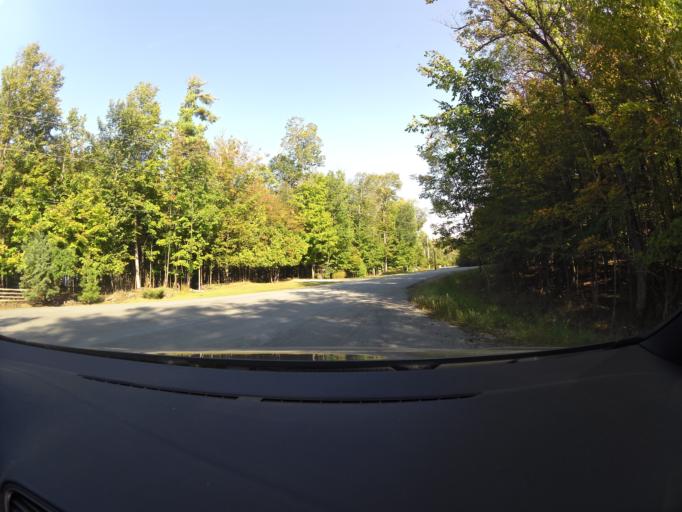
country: CA
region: Ontario
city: Arnprior
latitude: 45.4628
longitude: -76.2840
